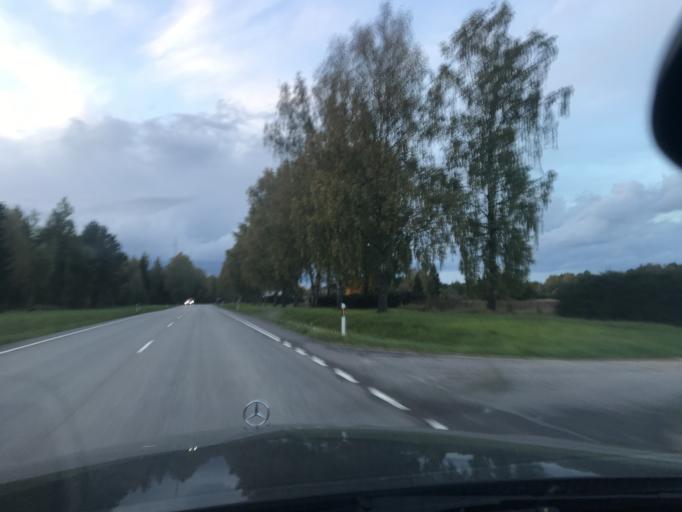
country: EE
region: Valgamaa
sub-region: Torva linn
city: Torva
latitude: 57.9855
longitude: 25.9431
